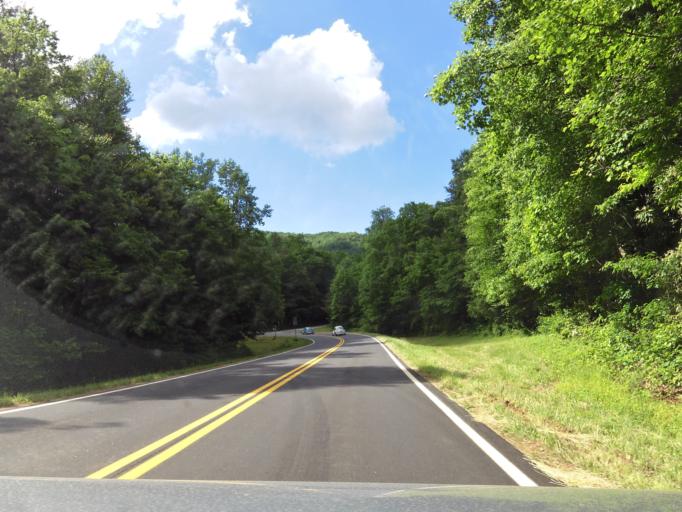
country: US
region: Georgia
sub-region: Towns County
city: Hiawassee
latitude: 34.8532
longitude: -83.7803
